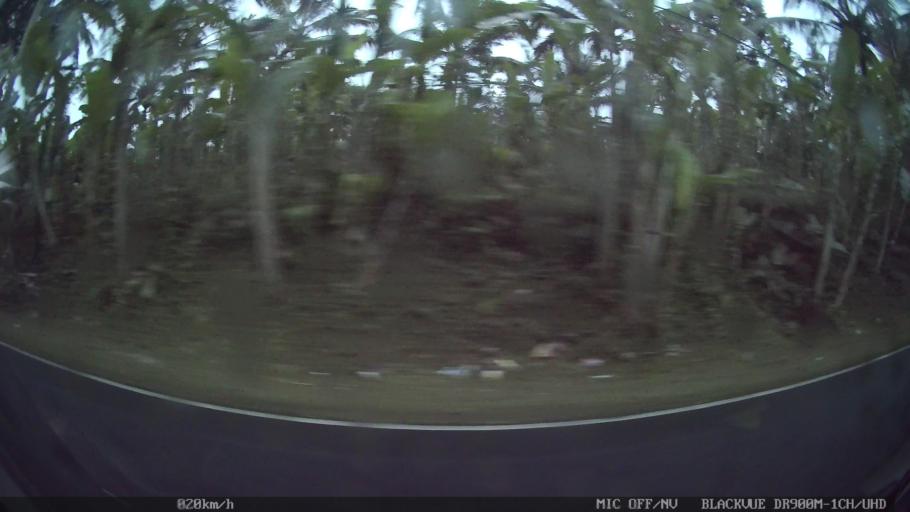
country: ID
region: Bali
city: Banjar Taro Kelod
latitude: -8.3665
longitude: 115.2705
